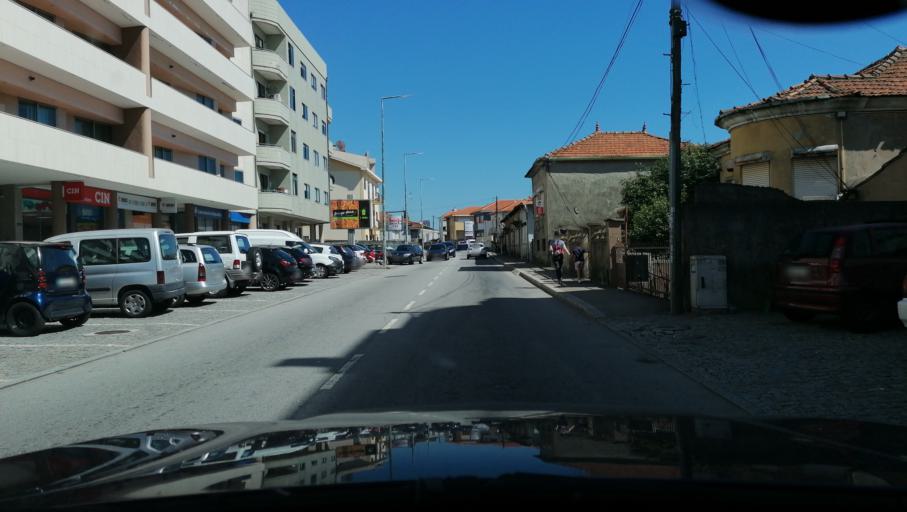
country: PT
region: Porto
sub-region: Vila Nova de Gaia
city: Canidelo
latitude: 41.1285
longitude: -8.6420
